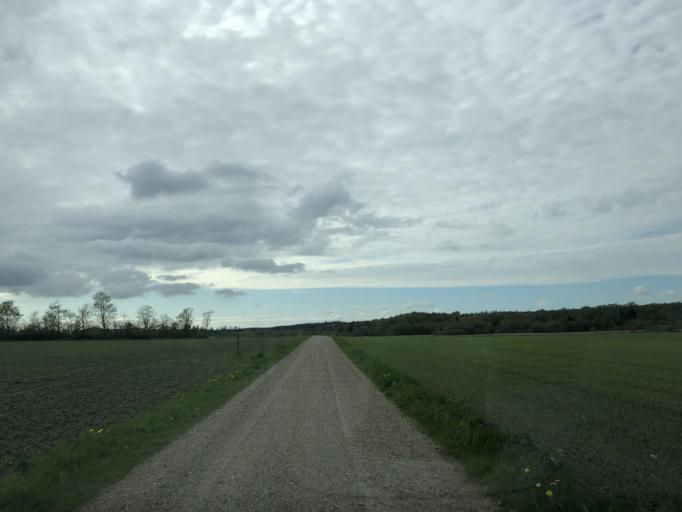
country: DK
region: Central Jutland
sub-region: Holstebro Kommune
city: Ulfborg
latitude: 56.1956
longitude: 8.4588
